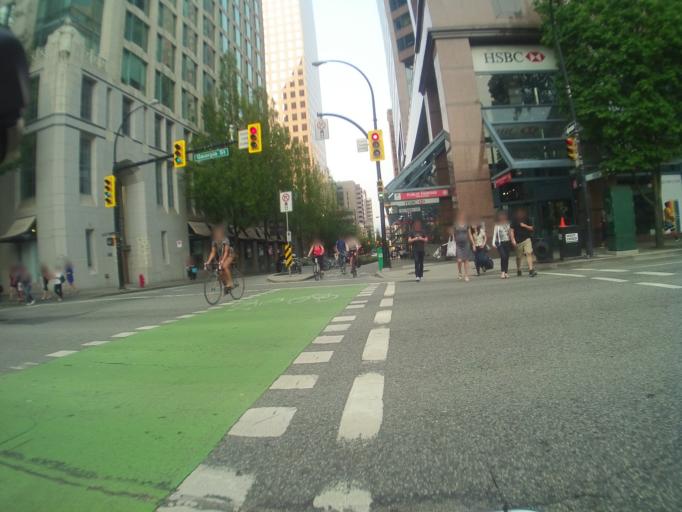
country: CA
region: British Columbia
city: West End
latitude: 49.2838
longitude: -123.1200
